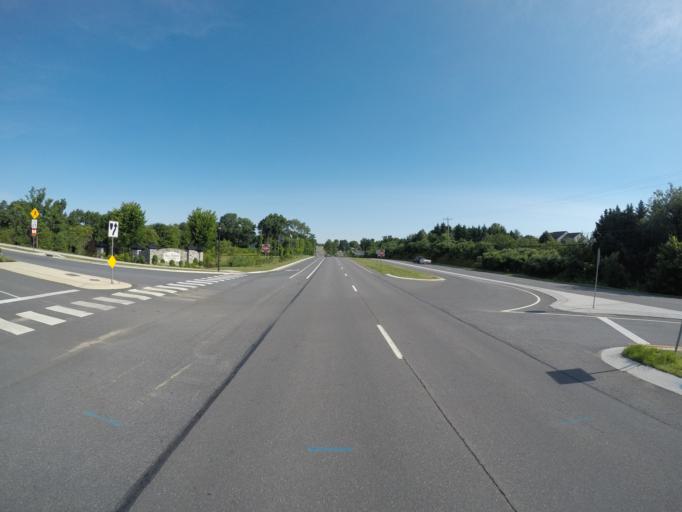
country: US
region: Delaware
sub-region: New Castle County
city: Bear
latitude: 39.5663
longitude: -75.6544
